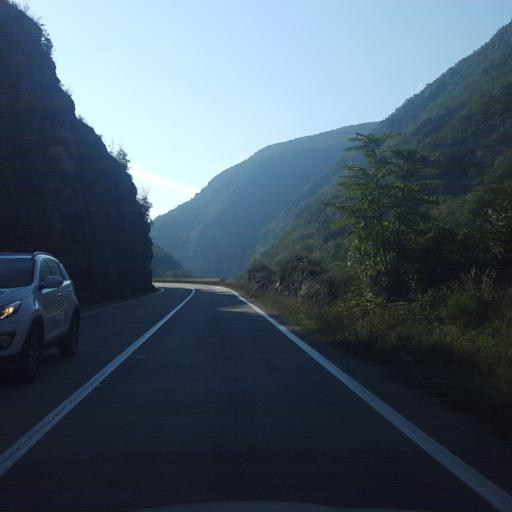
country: RS
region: Central Serbia
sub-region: Nisavski Okrug
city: Svrljig
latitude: 43.3330
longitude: 22.0954
